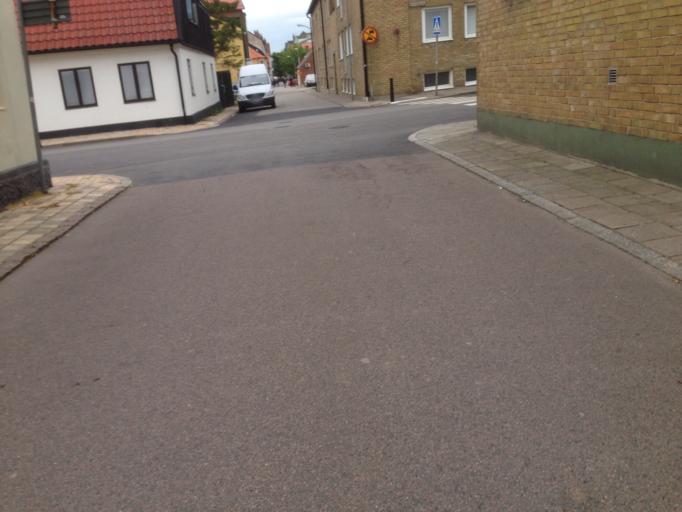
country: SE
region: Skane
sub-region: Landskrona
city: Landskrona
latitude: 55.8674
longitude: 12.8284
